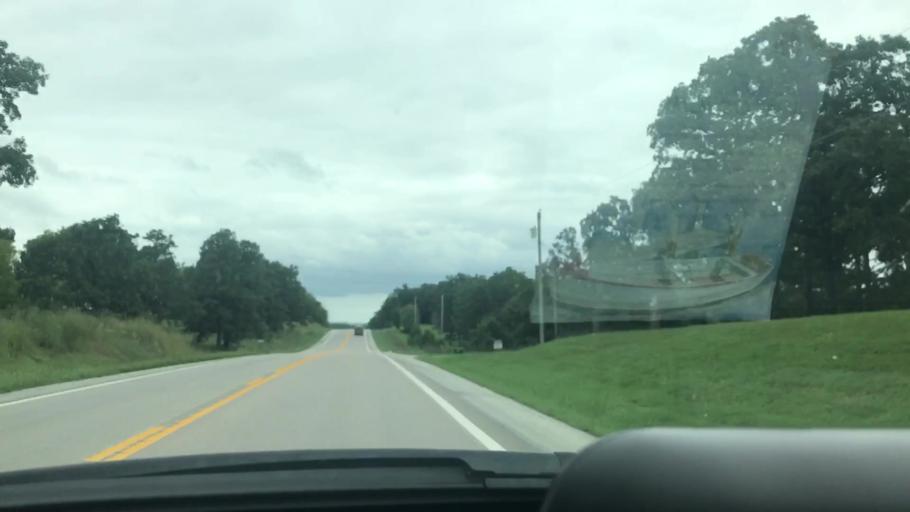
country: US
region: Missouri
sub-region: Dallas County
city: Buffalo
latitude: 37.7108
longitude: -93.1148
